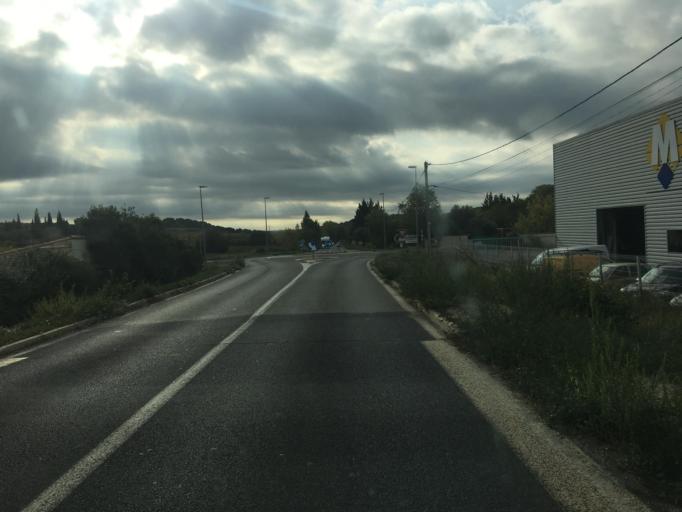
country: FR
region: Languedoc-Roussillon
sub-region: Departement de l'Herault
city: Nebian
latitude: 43.6024
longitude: 3.4389
